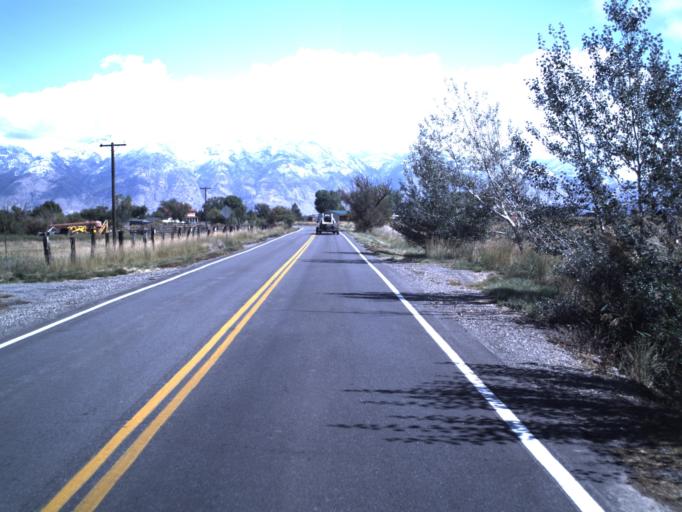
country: US
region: Utah
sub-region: Utah County
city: Benjamin
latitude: 40.1566
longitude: -111.7163
